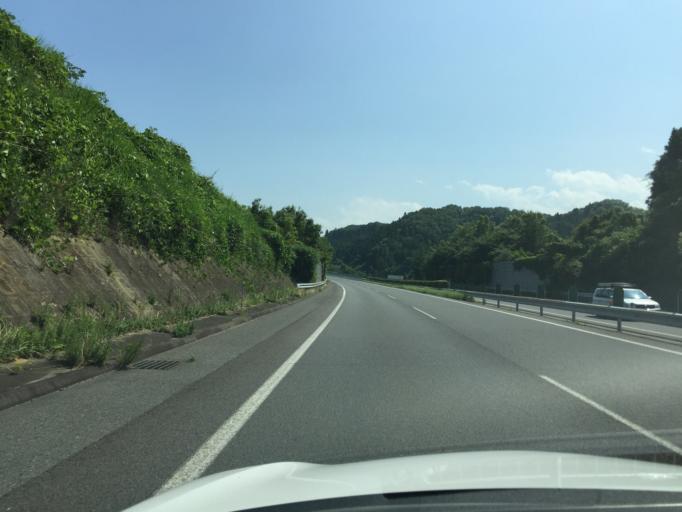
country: JP
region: Fukushima
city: Iwaki
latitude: 36.9989
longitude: 140.8071
